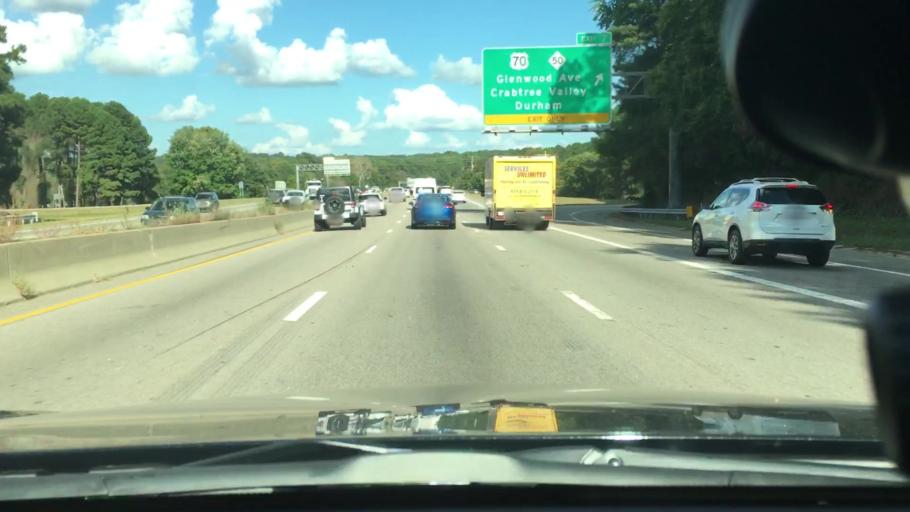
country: US
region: North Carolina
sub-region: Wake County
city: West Raleigh
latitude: 35.8341
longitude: -78.6728
